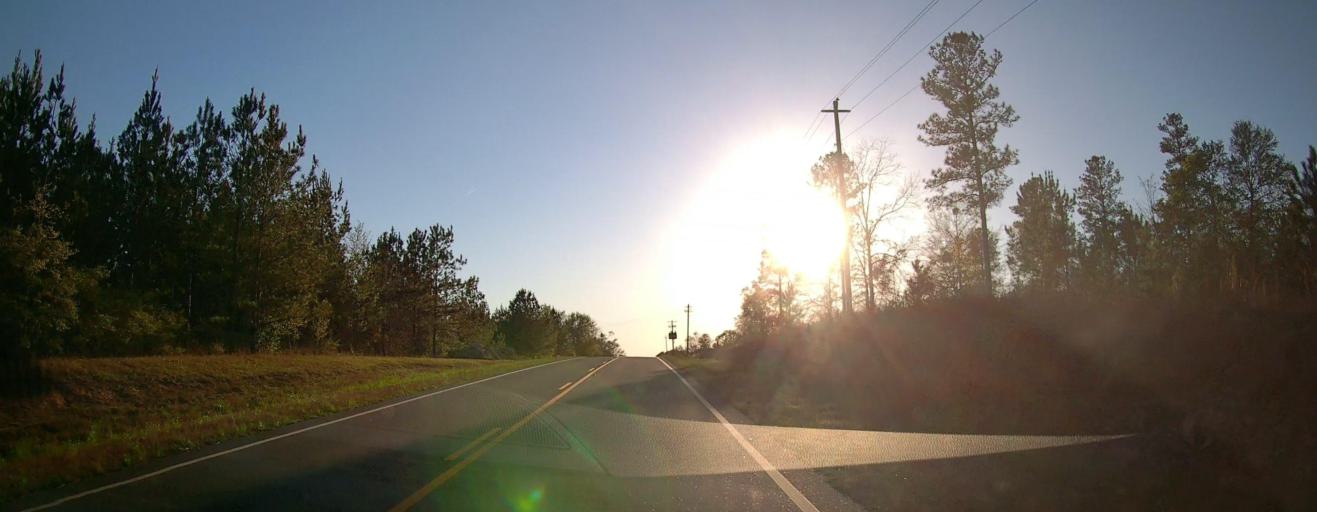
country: US
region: Georgia
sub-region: Wilcox County
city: Rochelle
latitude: 31.9675
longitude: -83.3824
